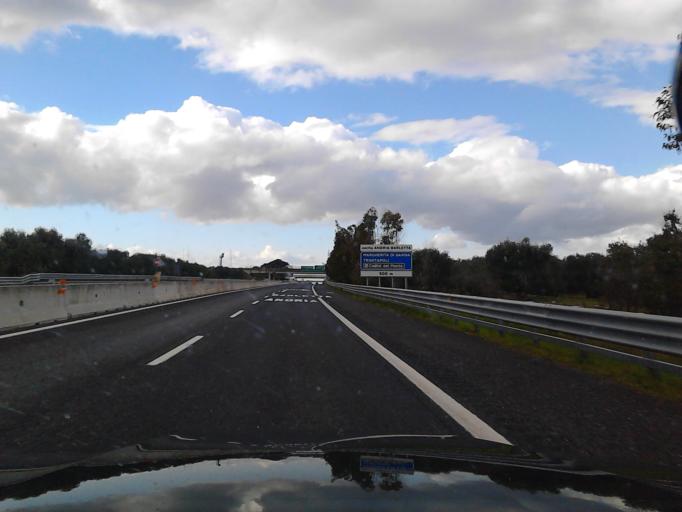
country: IT
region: Apulia
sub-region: Provincia di Barletta - Andria - Trani
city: Andria
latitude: 41.2530
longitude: 16.2970
